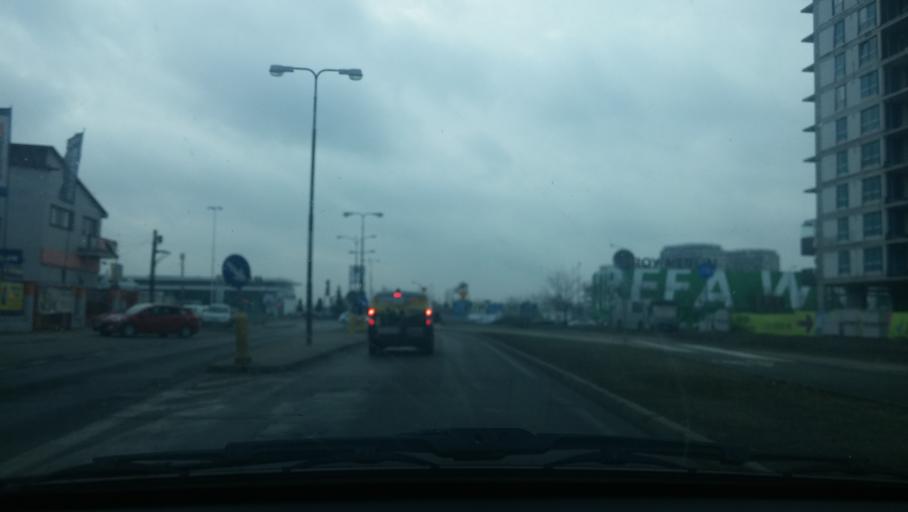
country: PL
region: Masovian Voivodeship
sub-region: Warszawa
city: Praga Poludnie
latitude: 52.2342
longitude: 21.1133
